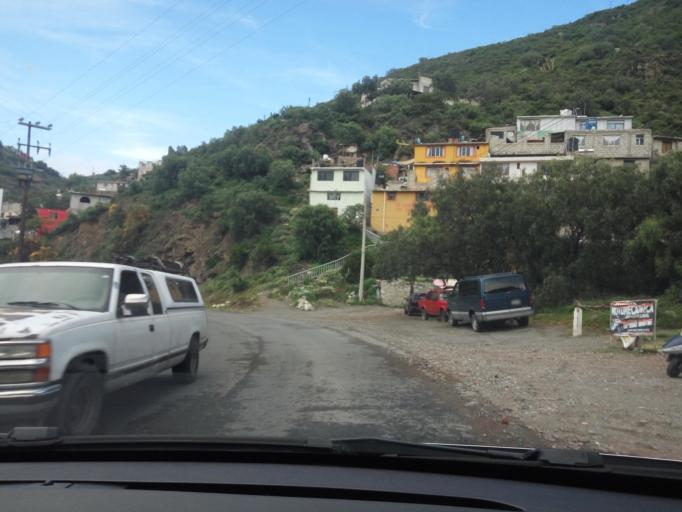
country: MX
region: Hidalgo
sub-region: Pachuca de Soto
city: Camelia (Barrio la Camelia)
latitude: 20.1354
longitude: -98.7240
